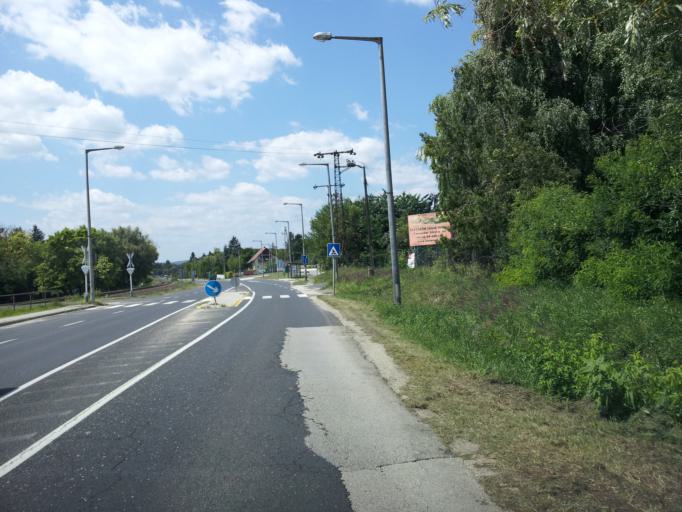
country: HU
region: Veszprem
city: Balatonkenese
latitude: 47.0323
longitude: 18.1246
